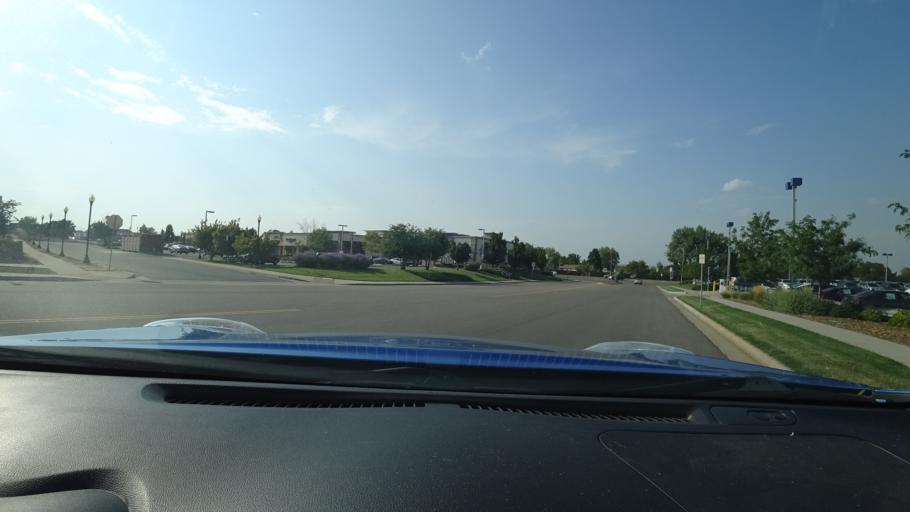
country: US
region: Colorado
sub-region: Adams County
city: Northglenn
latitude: 39.8841
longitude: -105.0193
